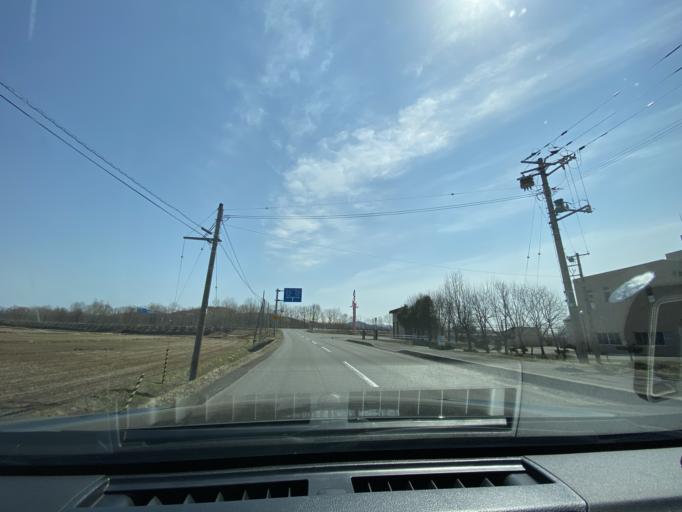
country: JP
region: Hokkaido
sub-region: Asahikawa-shi
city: Asahikawa
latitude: 43.8976
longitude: 142.5249
